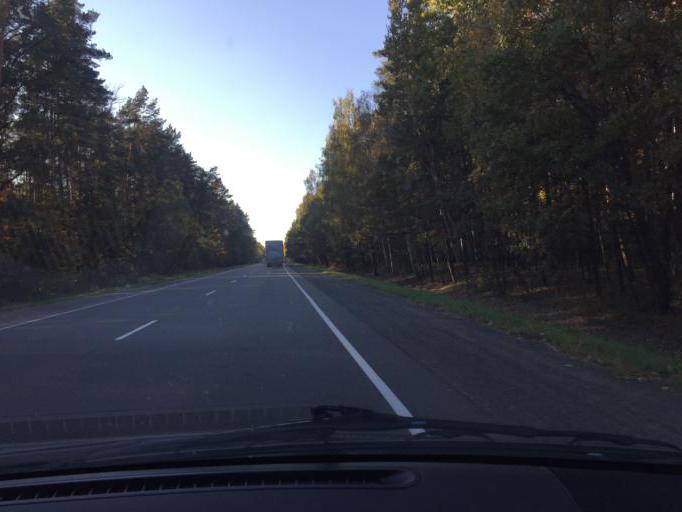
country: BY
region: Brest
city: Horad Luninyets
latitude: 52.2863
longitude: 26.7974
